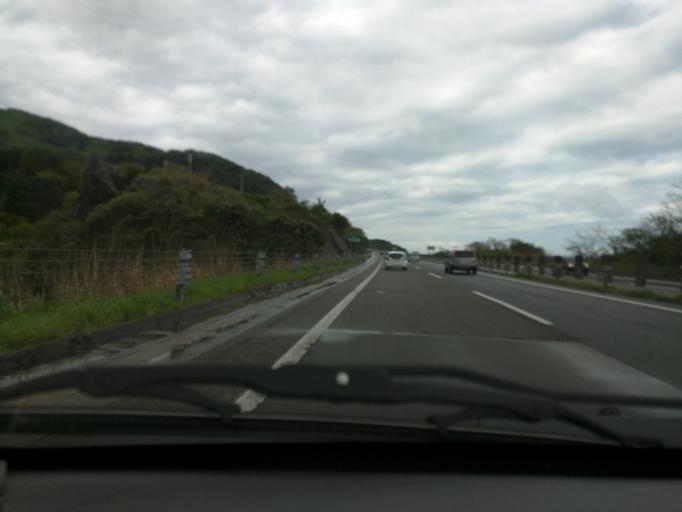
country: JP
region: Niigata
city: Kashiwazaki
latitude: 37.3101
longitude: 138.4252
